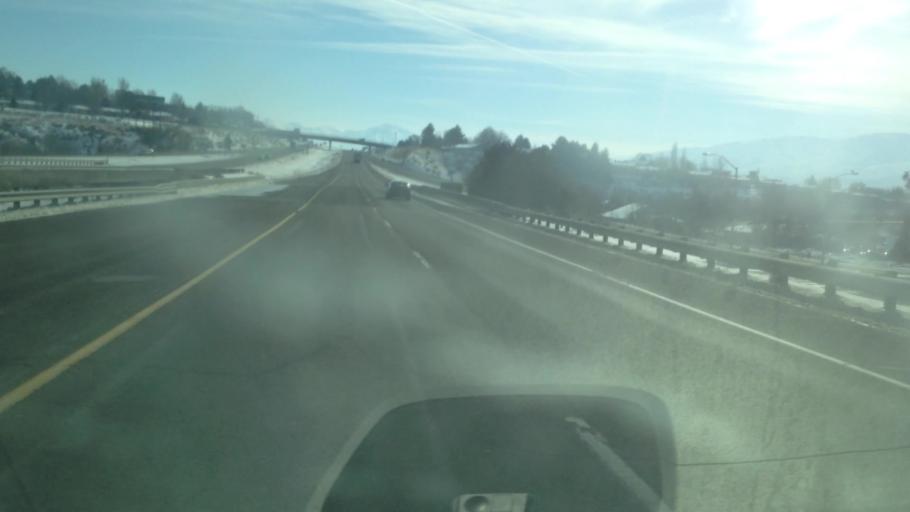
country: US
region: Idaho
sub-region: Bannock County
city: Pocatello
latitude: 42.8984
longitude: -112.4363
